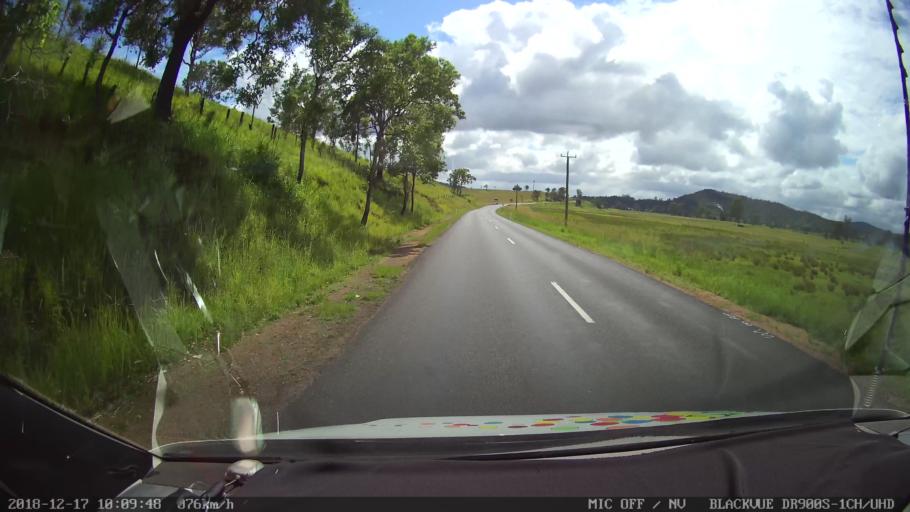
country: AU
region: New South Wales
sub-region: Clarence Valley
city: Gordon
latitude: -28.8875
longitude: 152.5485
